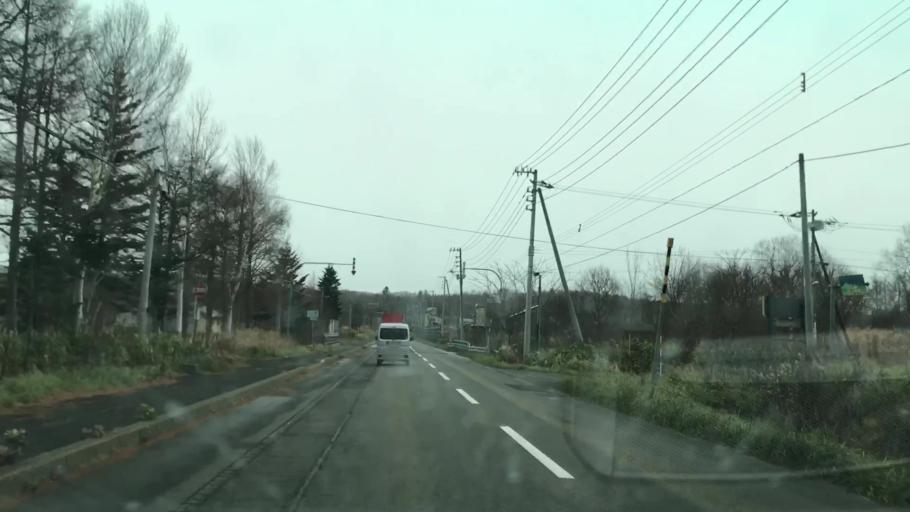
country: JP
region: Hokkaido
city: Yoichi
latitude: 43.3081
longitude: 140.5531
